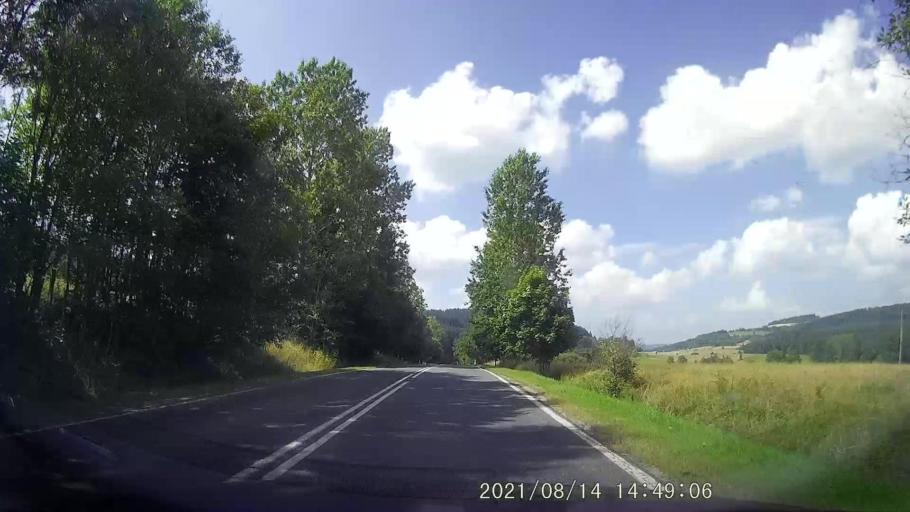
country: PL
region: Lower Silesian Voivodeship
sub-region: Powiat walbrzyski
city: Gluszyca Gorna
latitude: 50.6384
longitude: 16.3894
